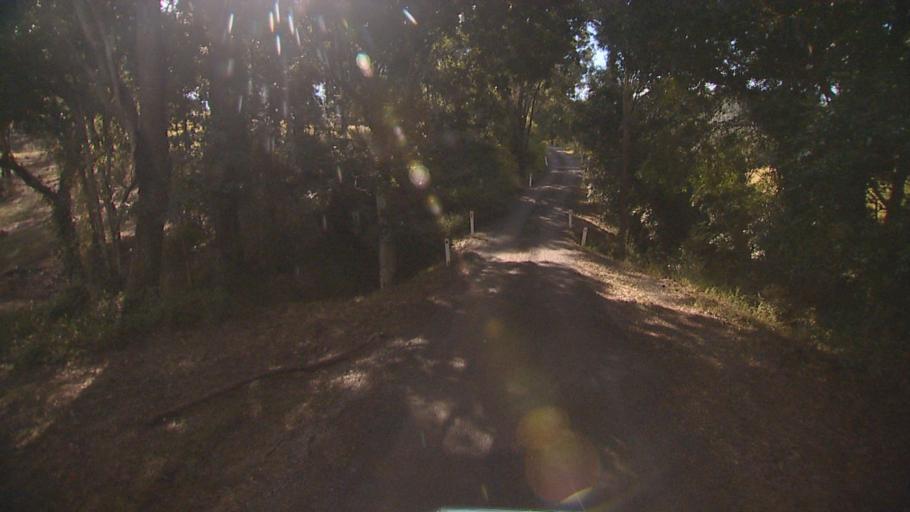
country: AU
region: Queensland
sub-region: Logan
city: Windaroo
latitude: -27.7738
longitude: 153.1735
